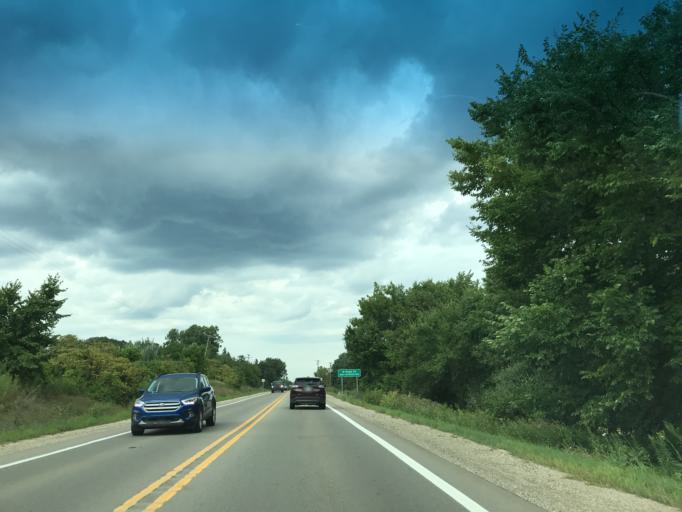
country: US
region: Michigan
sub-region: Oakland County
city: Milford
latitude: 42.5335
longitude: -83.6167
